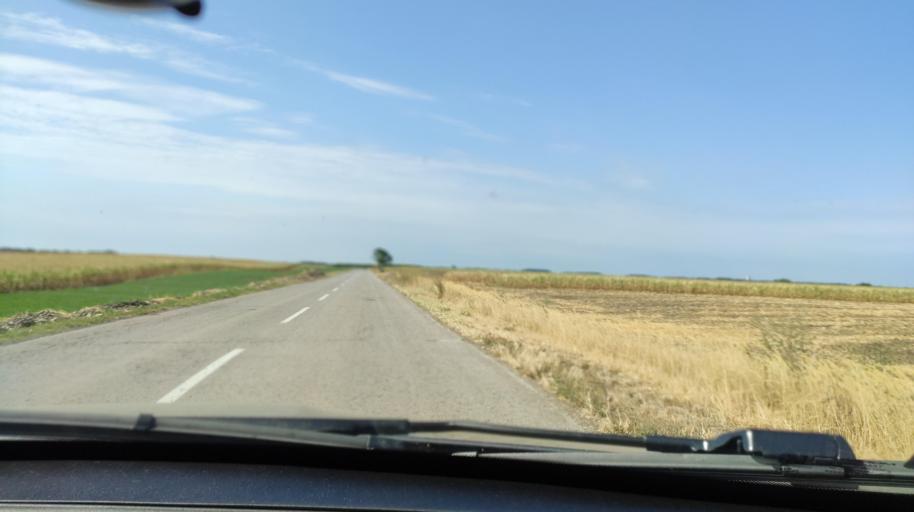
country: RS
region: Autonomna Pokrajina Vojvodina
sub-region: Severnobacki Okrug
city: Backa Topola
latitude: 45.8483
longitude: 19.5619
